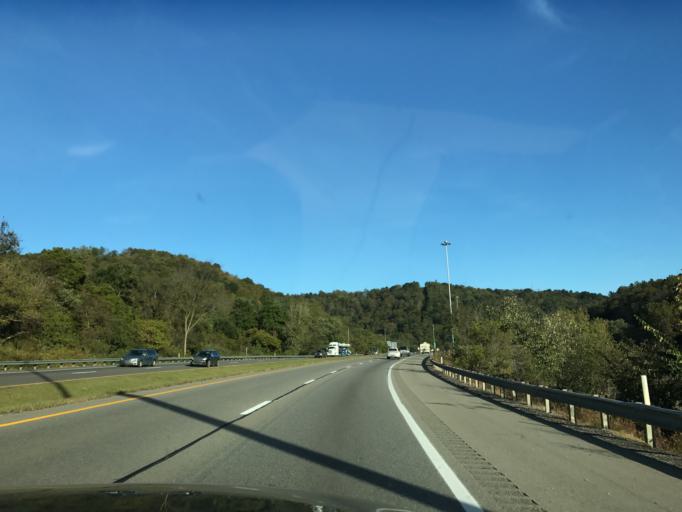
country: US
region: West Virginia
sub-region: Ohio County
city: Bethlehem
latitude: 40.0445
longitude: -80.6191
